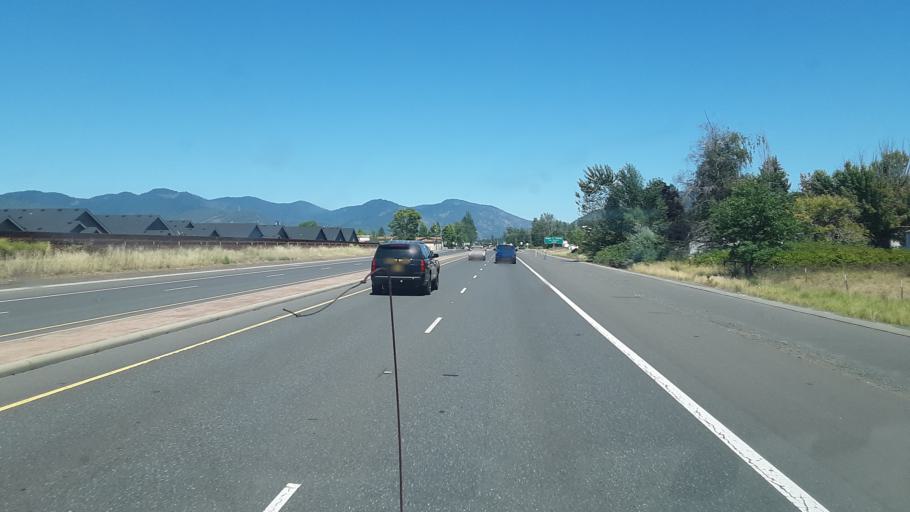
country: US
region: Oregon
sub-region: Josephine County
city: Redwood
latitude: 42.4155
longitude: -123.3805
